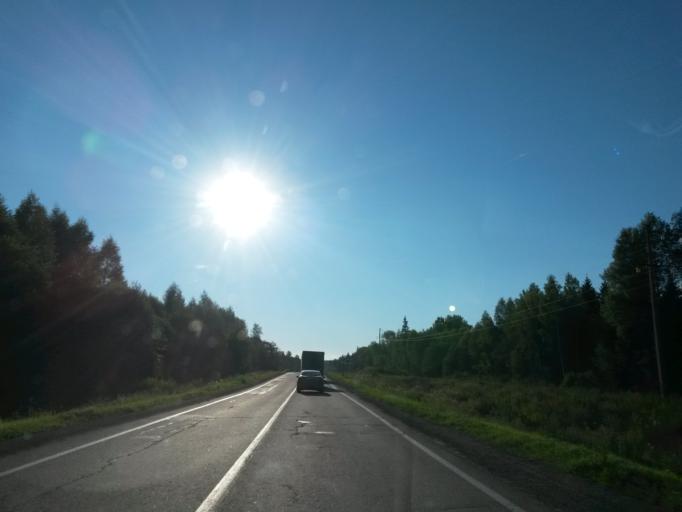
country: RU
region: Jaroslavl
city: Gavrilov-Yam
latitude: 57.2643
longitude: 40.0164
